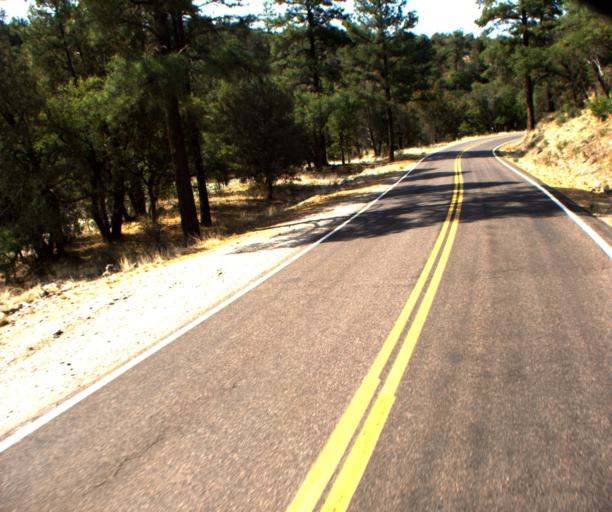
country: US
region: Arizona
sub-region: Greenlee County
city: Clifton
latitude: 33.1024
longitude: -109.0675
